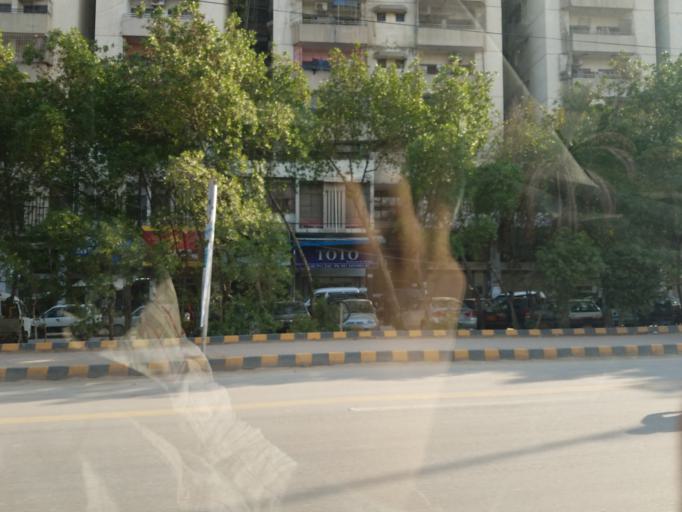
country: PK
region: Sindh
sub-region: Karachi District
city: Karachi
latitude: 24.8633
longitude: 67.0737
